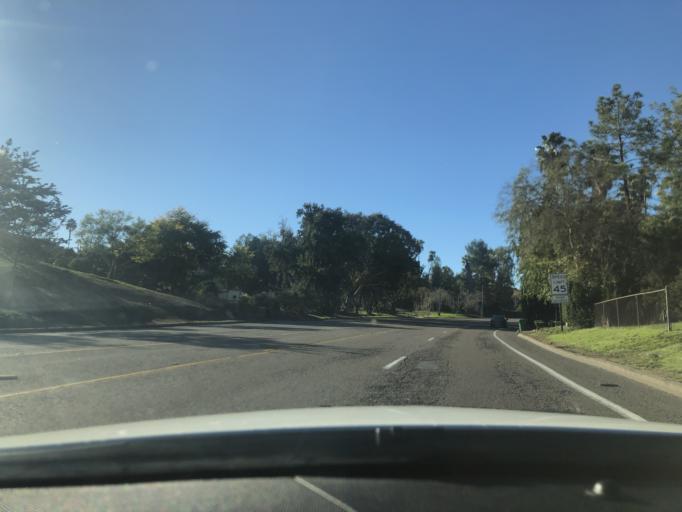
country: US
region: California
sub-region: San Diego County
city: Casa de Oro-Mount Helix
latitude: 32.7674
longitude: -116.9589
